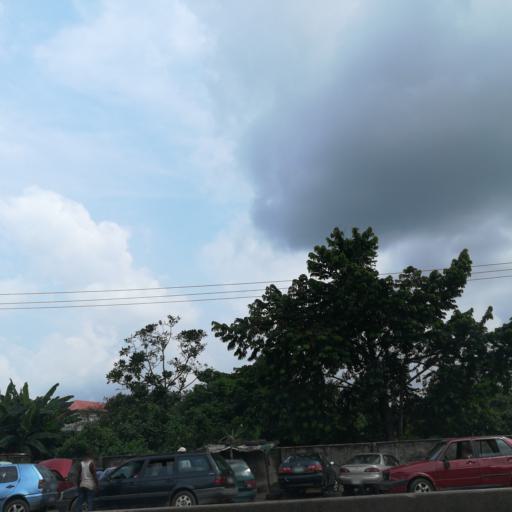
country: NG
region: Rivers
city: Port Harcourt
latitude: 4.8528
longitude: 7.0698
